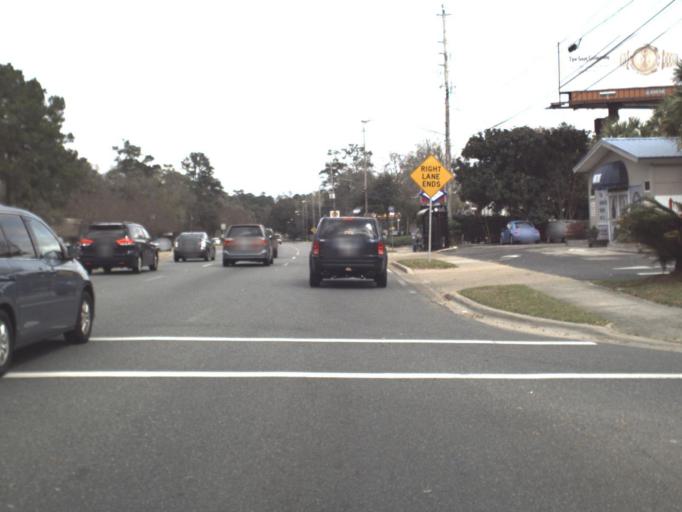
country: US
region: Florida
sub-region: Leon County
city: Tallahassee
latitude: 30.4665
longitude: -84.2684
